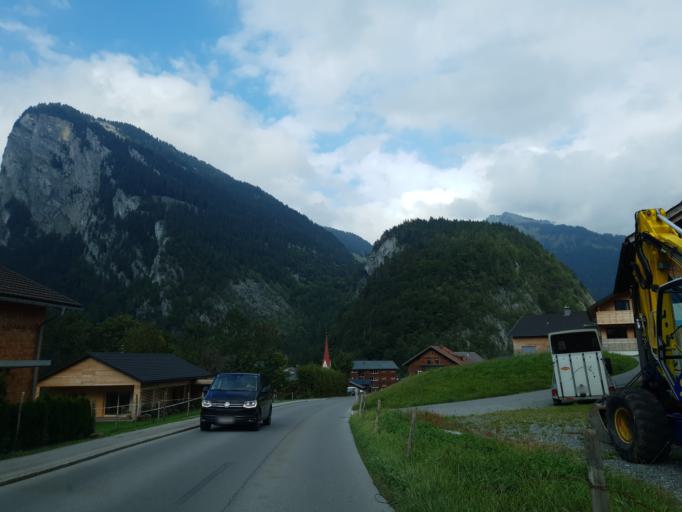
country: AT
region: Vorarlberg
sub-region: Politischer Bezirk Bregenz
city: Au
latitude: 47.3213
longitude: 9.9736
